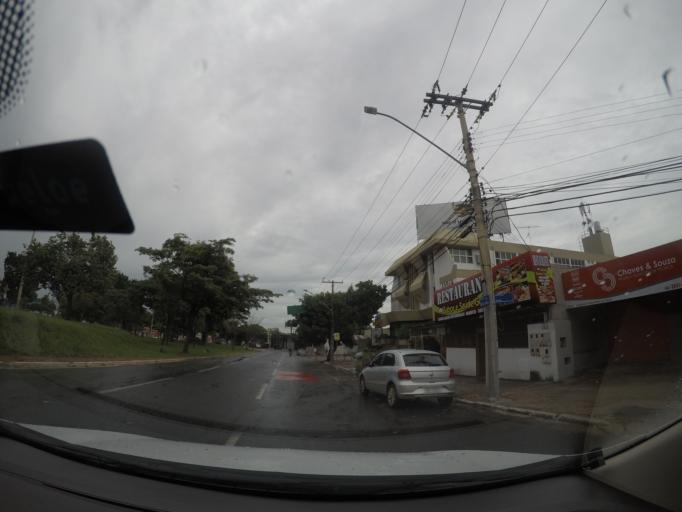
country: BR
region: Goias
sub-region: Goiania
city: Goiania
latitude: -16.6904
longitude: -49.2527
